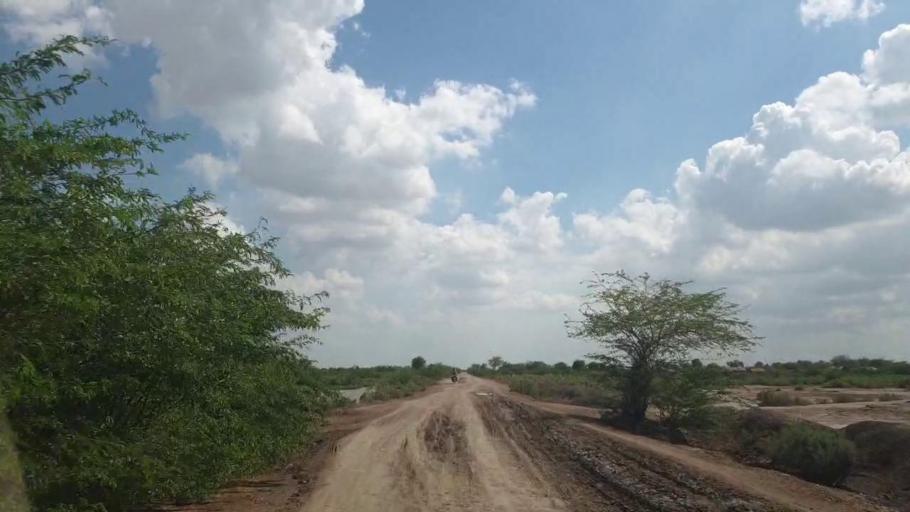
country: PK
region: Sindh
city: Pithoro
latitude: 25.6086
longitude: 69.4093
